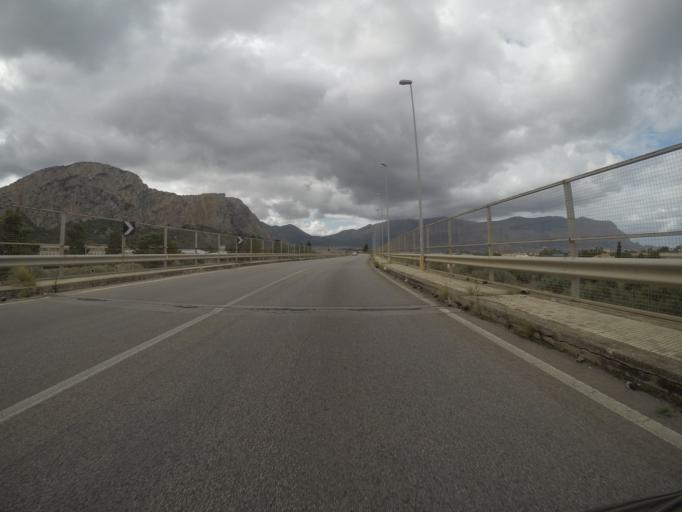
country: IT
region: Sicily
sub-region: Palermo
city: Capaci
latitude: 38.1661
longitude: 13.2216
